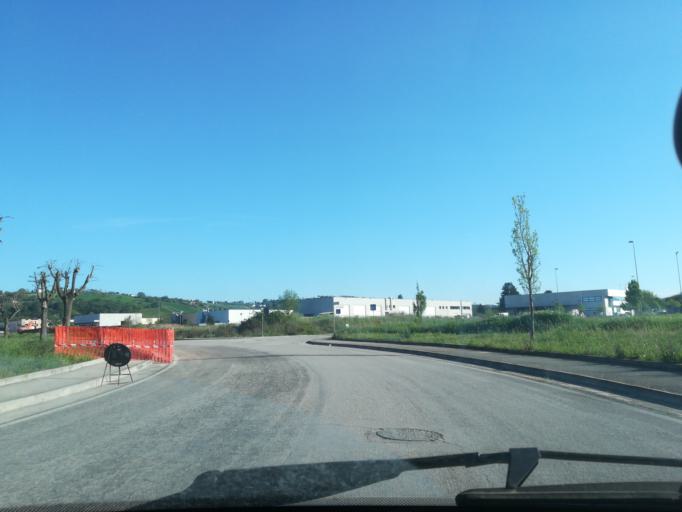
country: IT
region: The Marches
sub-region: Provincia di Macerata
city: Zona Industriale
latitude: 43.2606
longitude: 13.4839
